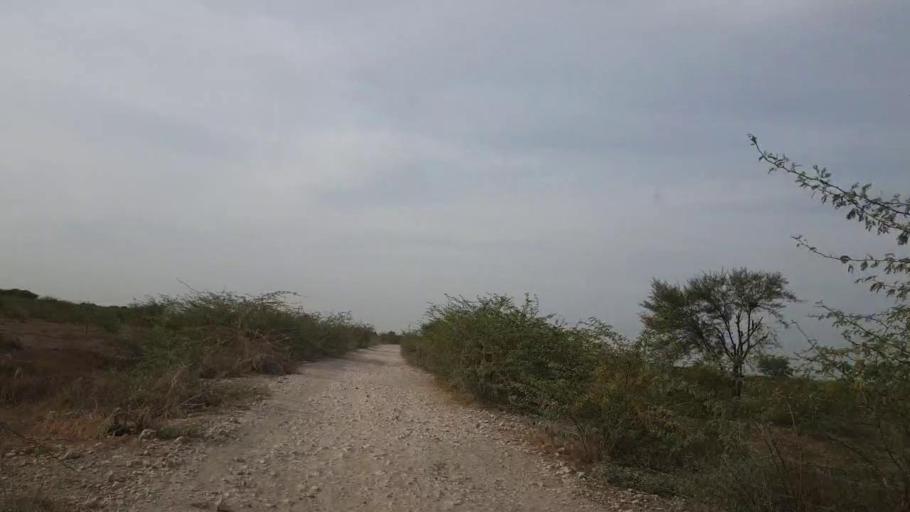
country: PK
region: Sindh
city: Nabisar
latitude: 24.9987
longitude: 69.5435
